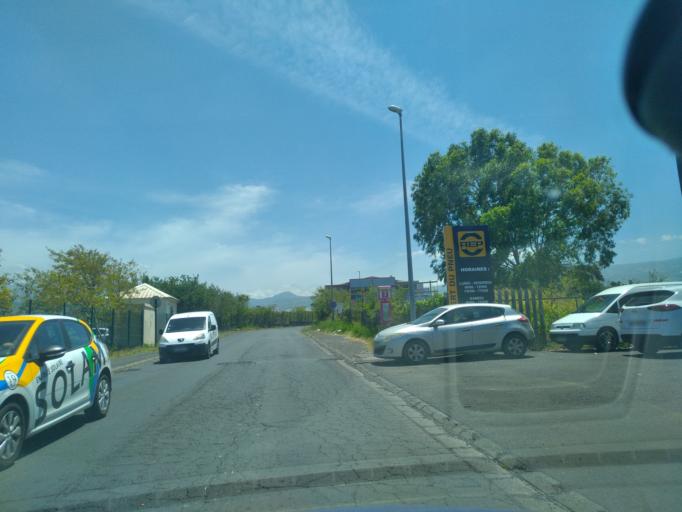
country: RE
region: Reunion
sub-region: Reunion
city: Saint-Pierre
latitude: -21.3213
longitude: 55.4493
